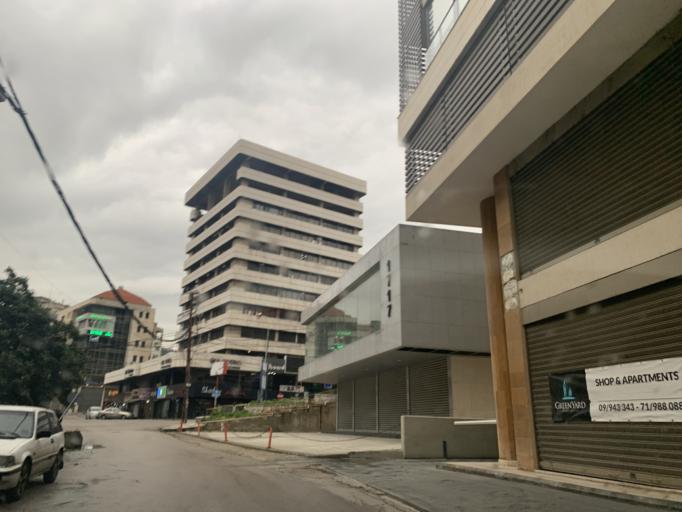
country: LB
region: Mont-Liban
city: Djounie
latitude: 33.9813
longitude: 35.6260
